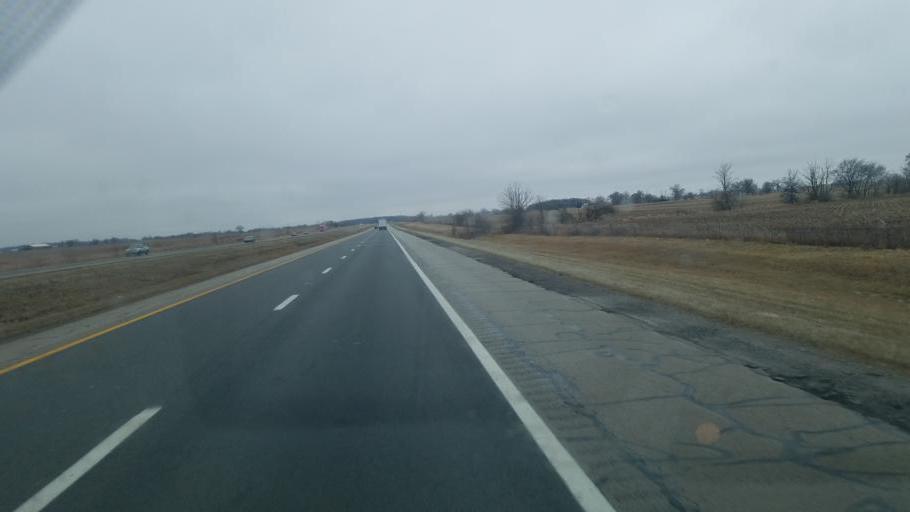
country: US
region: Ohio
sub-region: Madison County
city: Bethel
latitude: 39.7208
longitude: -83.4008
